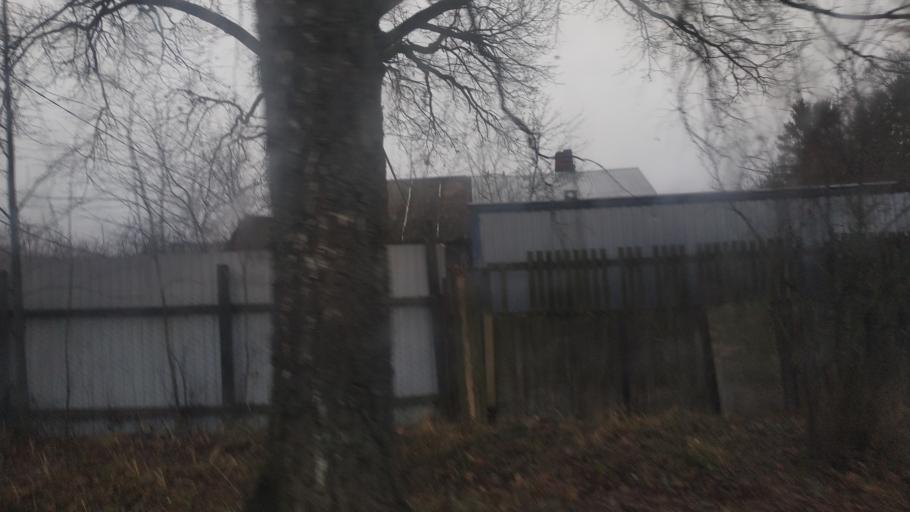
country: RU
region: Moskovskaya
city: Lugovaya
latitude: 56.0547
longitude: 37.4762
